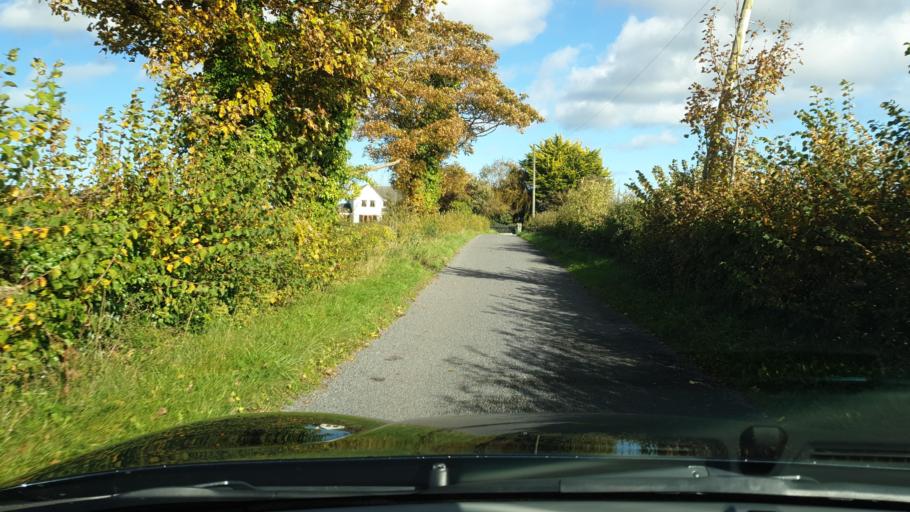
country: IE
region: Leinster
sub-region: Fingal County
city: Swords
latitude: 53.4948
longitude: -6.2500
